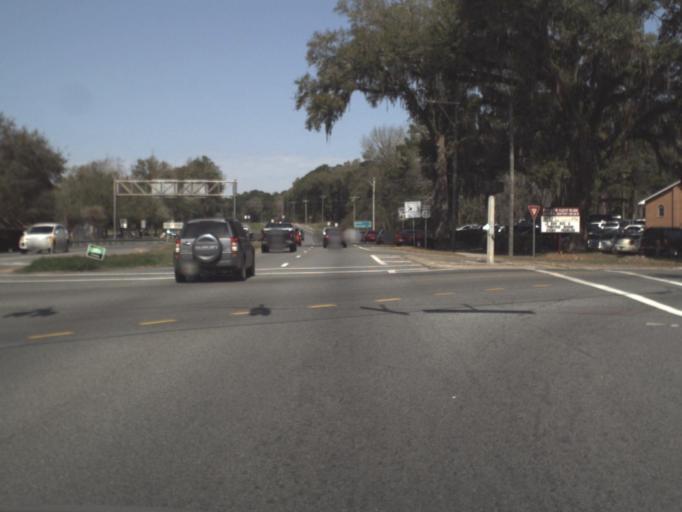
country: US
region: Florida
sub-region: Gadsden County
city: Midway
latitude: 30.5323
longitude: -84.3617
